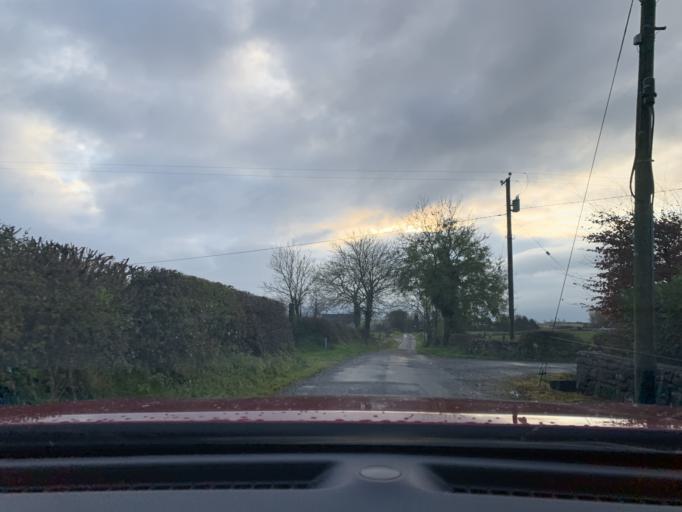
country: IE
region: Connaught
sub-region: Sligo
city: Ballymote
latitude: 54.0359
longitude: -8.5397
